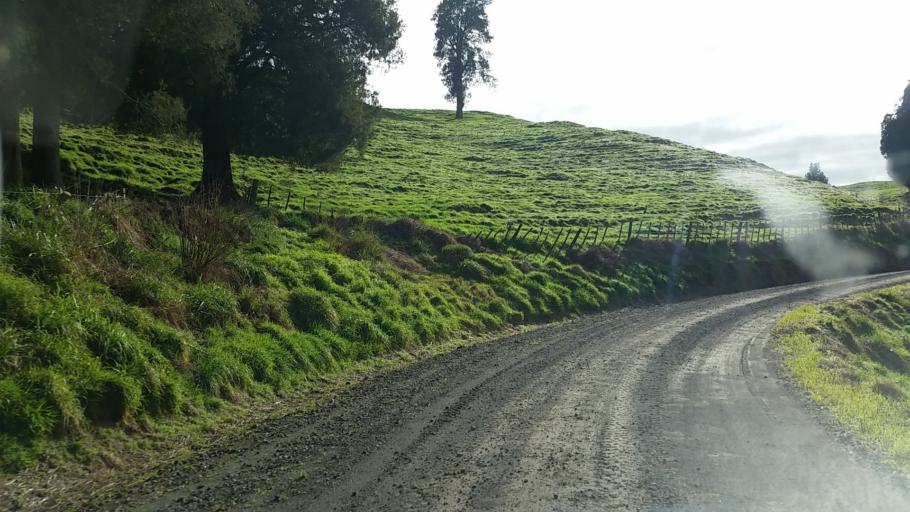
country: NZ
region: Taranaki
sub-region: South Taranaki District
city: Eltham
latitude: -39.2562
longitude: 174.5184
